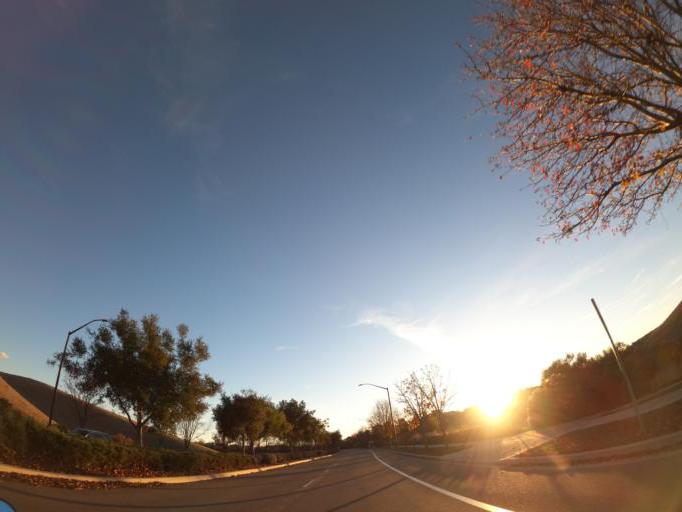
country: US
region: California
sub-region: Contra Costa County
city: Blackhawk
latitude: 37.7560
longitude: -121.8880
